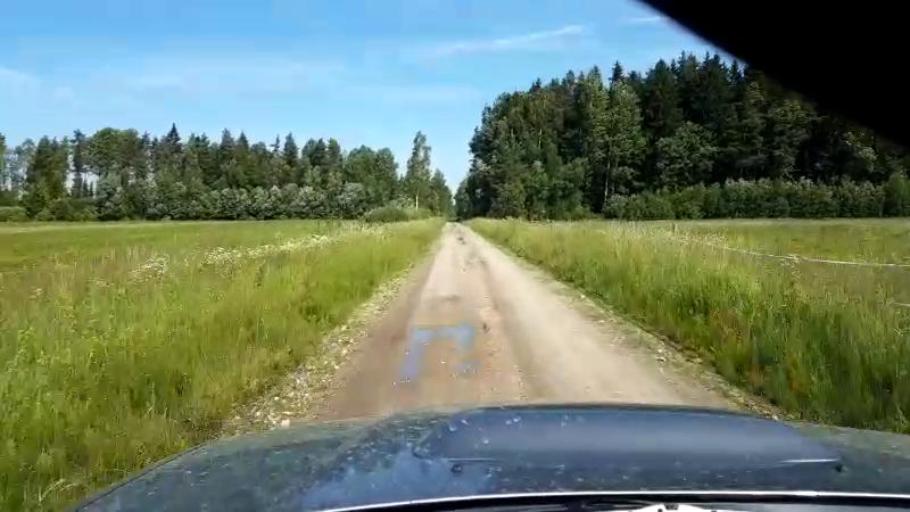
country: EE
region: Paernumaa
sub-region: Sindi linn
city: Sindi
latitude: 58.5188
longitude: 24.6609
